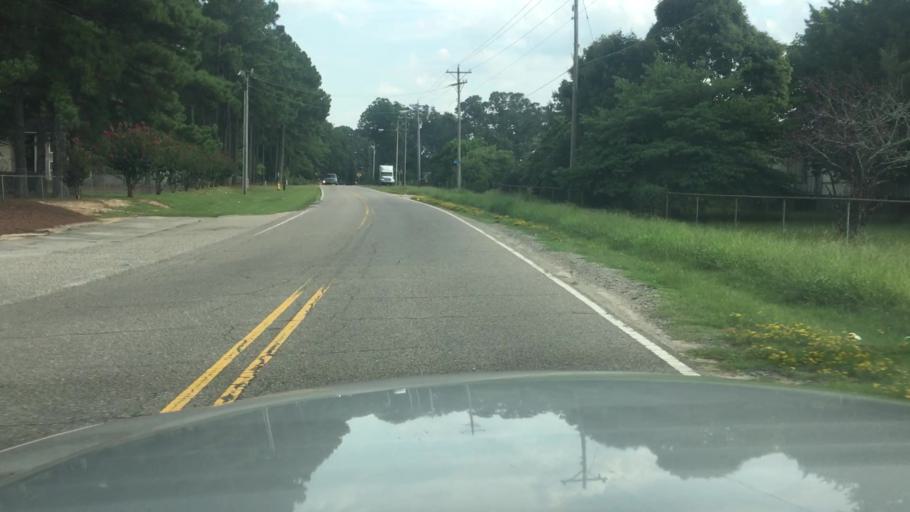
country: US
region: North Carolina
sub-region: Cumberland County
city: Fayetteville
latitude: 35.0913
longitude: -78.9430
